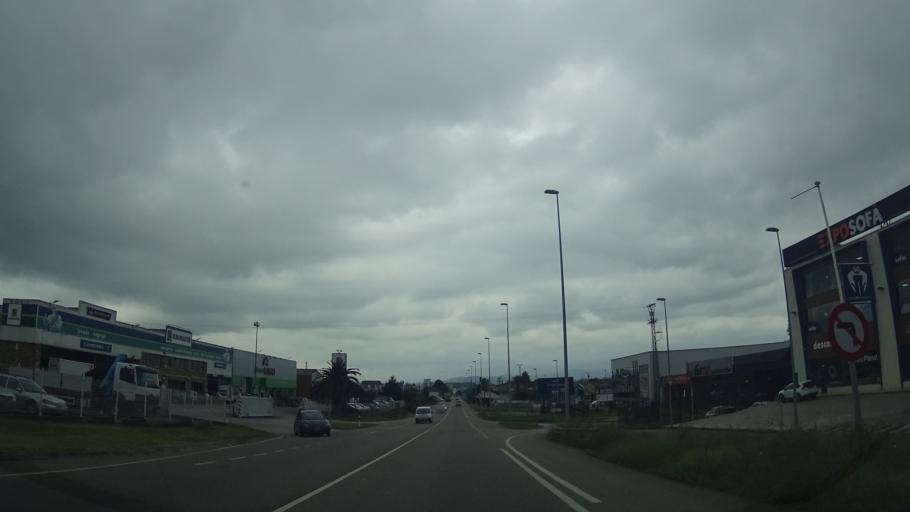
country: ES
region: Asturias
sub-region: Province of Asturias
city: Lugones
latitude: 43.3838
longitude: -5.7666
